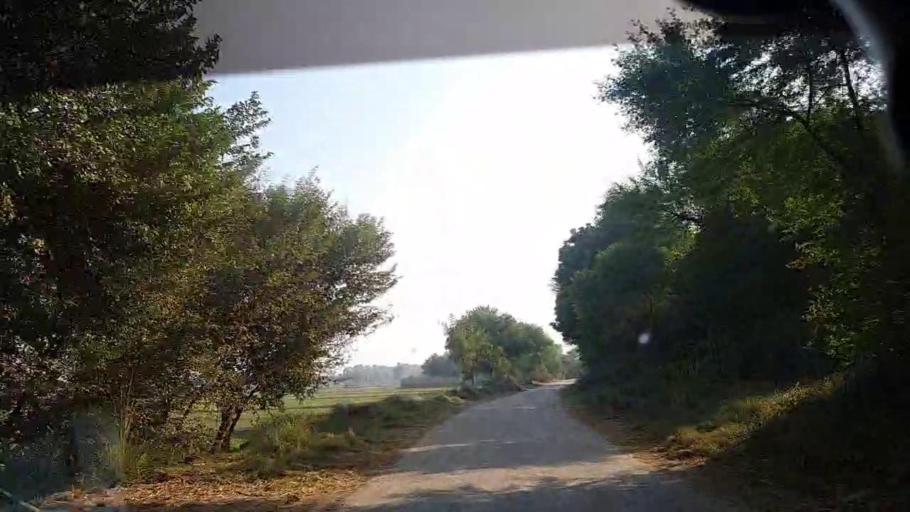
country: PK
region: Sindh
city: Hingorja
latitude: 27.2236
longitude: 68.2699
